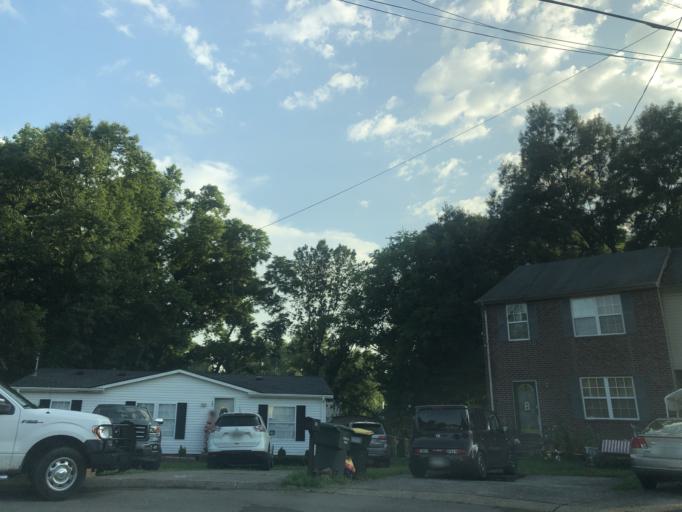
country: US
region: Tennessee
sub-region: Davidson County
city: Lakewood
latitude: 36.1467
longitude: -86.6421
